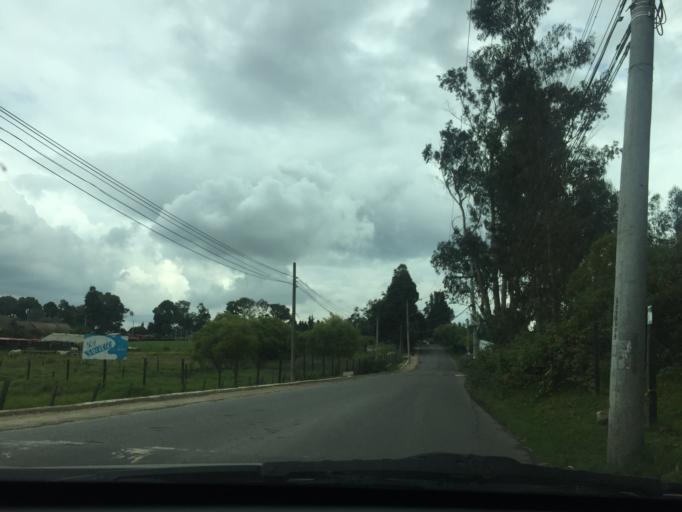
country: CO
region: Cundinamarca
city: Chia
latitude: 4.8343
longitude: -74.0713
